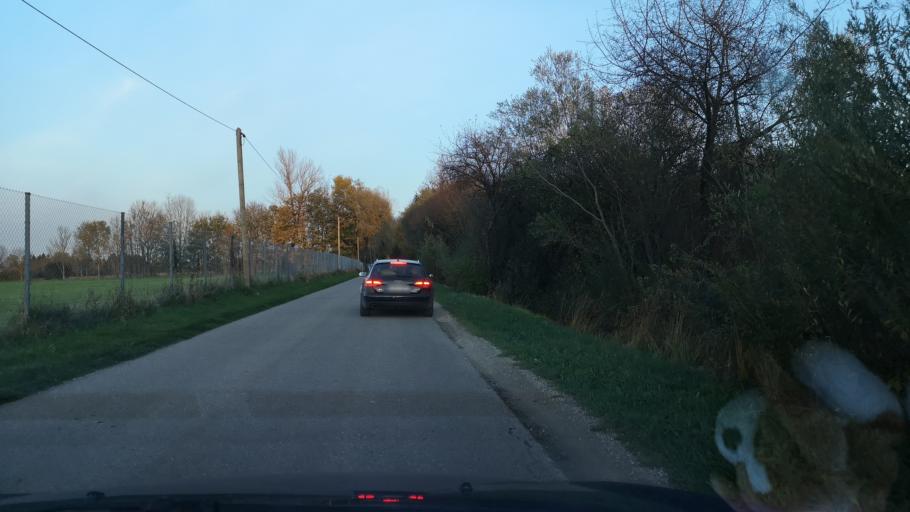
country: DE
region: Bavaria
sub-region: Upper Bavaria
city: Eichenried
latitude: 48.2462
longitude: 11.7460
